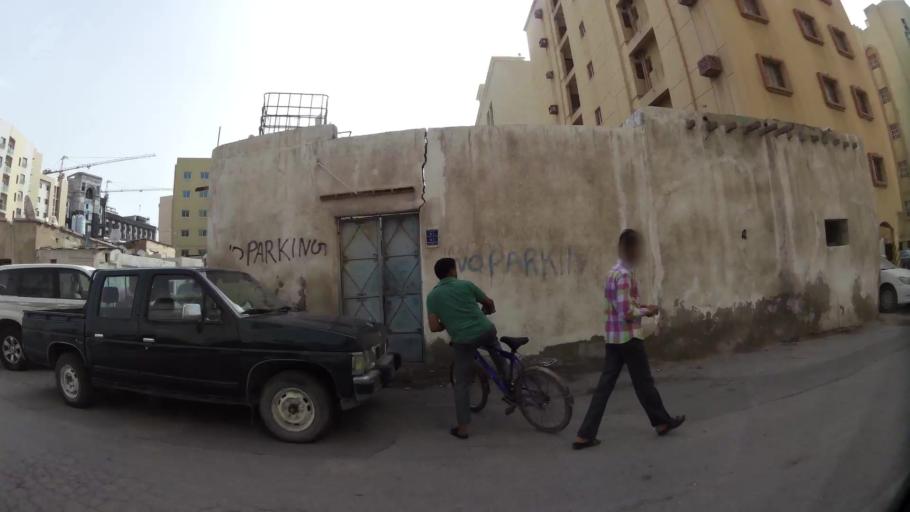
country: QA
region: Baladiyat ad Dawhah
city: Doha
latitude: 25.2783
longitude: 51.5499
